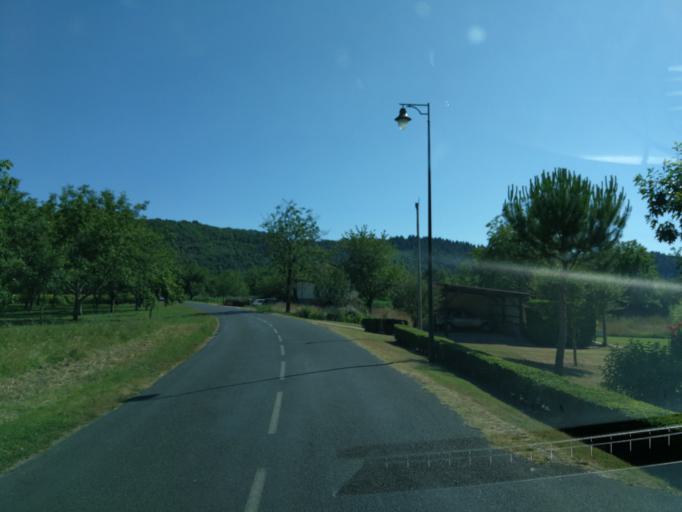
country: FR
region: Midi-Pyrenees
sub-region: Departement du Lot
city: Souillac
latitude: 44.8730
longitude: 1.4425
